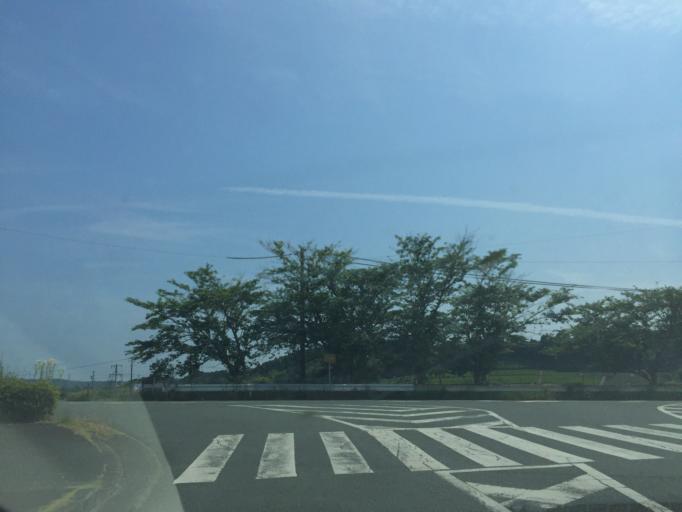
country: JP
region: Shizuoka
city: Fukuroi
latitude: 34.7840
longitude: 137.9530
